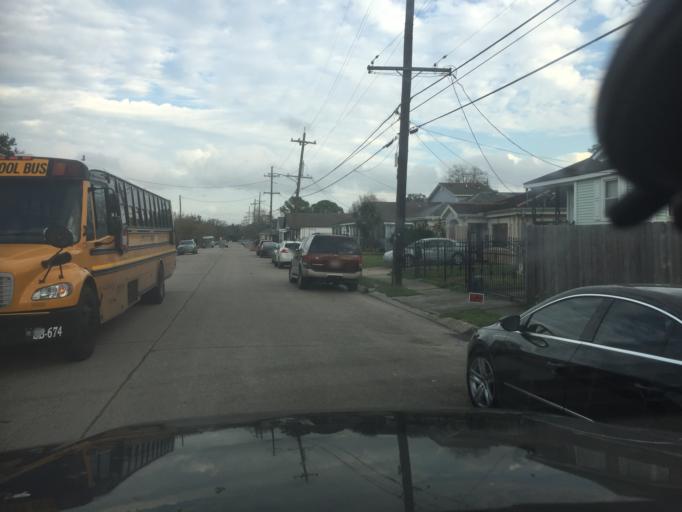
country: US
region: Louisiana
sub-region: Orleans Parish
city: New Orleans
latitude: 29.9877
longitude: -90.0806
